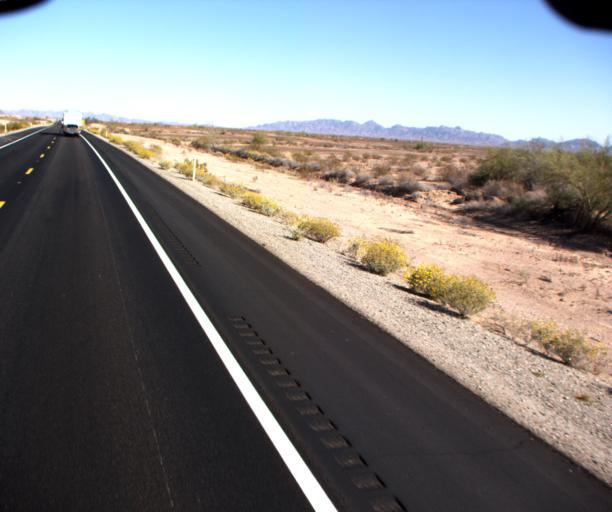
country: US
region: Arizona
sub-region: Yuma County
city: Wellton
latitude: 33.0102
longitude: -114.2853
